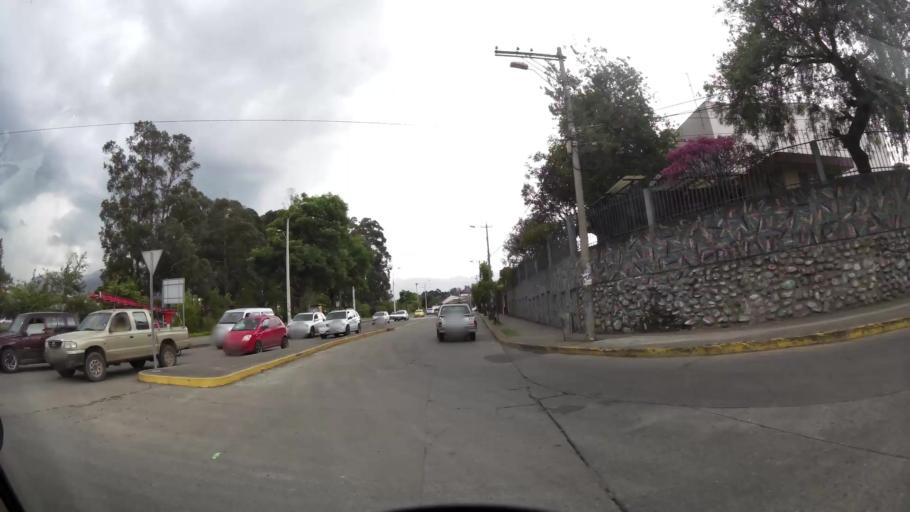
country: EC
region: Azuay
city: Cuenca
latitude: -2.8954
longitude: -79.0153
